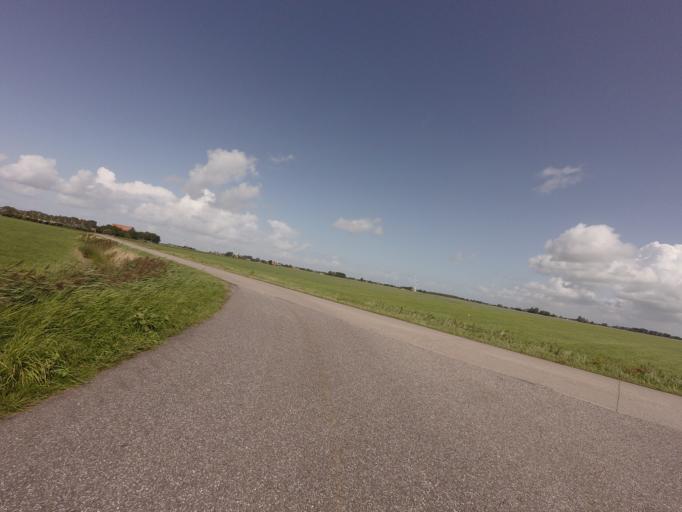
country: NL
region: Friesland
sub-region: Sudwest Fryslan
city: Makkum
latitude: 53.0676
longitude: 5.4570
